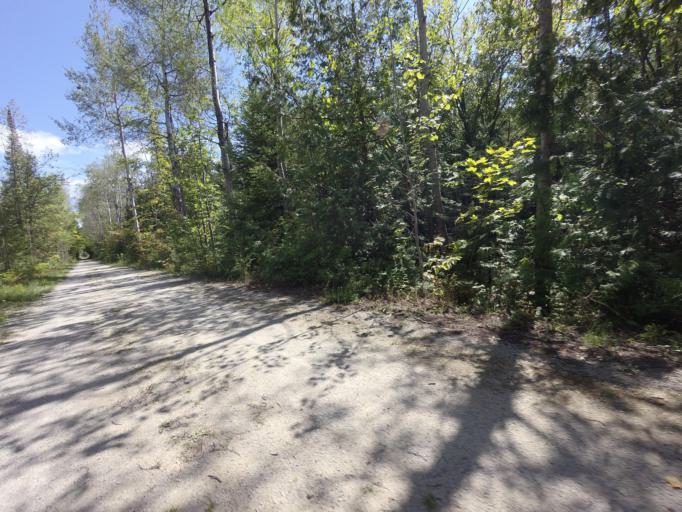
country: CA
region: Ontario
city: Orangeville
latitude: 43.7778
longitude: -80.1184
